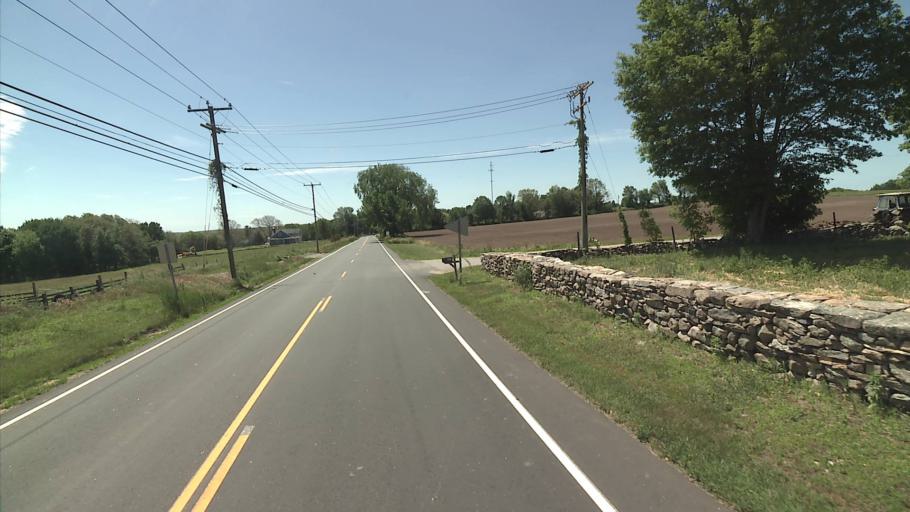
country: US
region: Connecticut
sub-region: Windham County
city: Moosup
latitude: 41.6665
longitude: -71.8472
